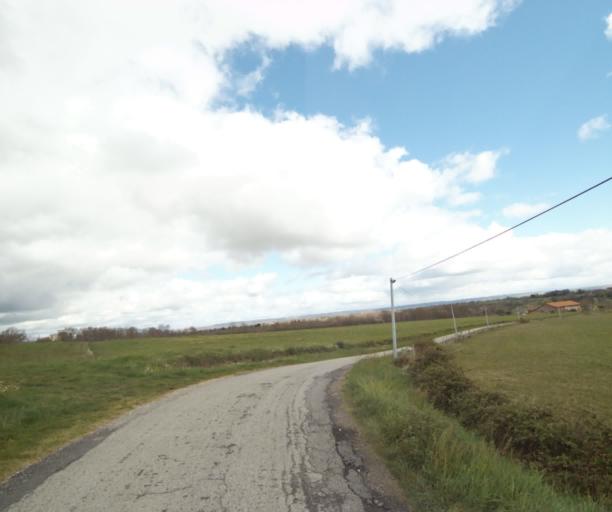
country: FR
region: Midi-Pyrenees
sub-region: Departement de l'Ariege
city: Saverdun
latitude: 43.2087
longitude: 1.5670
